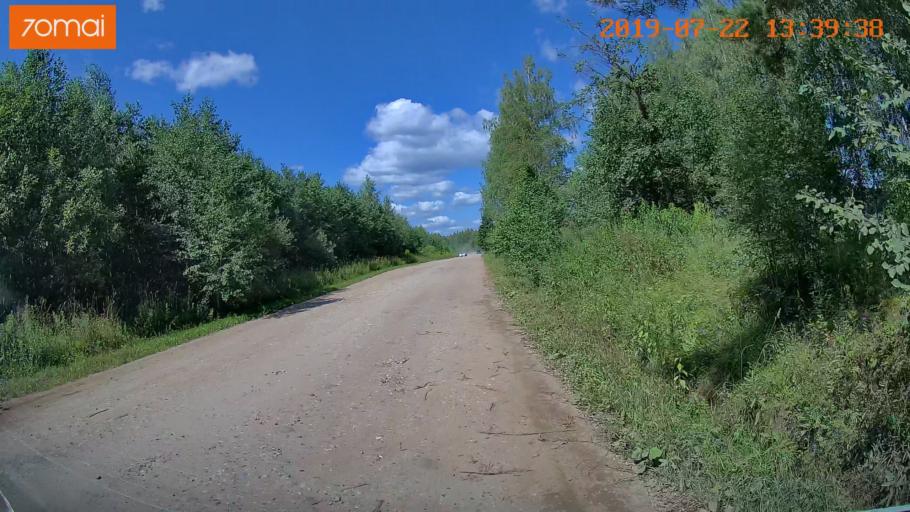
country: RU
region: Ivanovo
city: Novo-Talitsy
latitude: 57.0734
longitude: 40.8817
